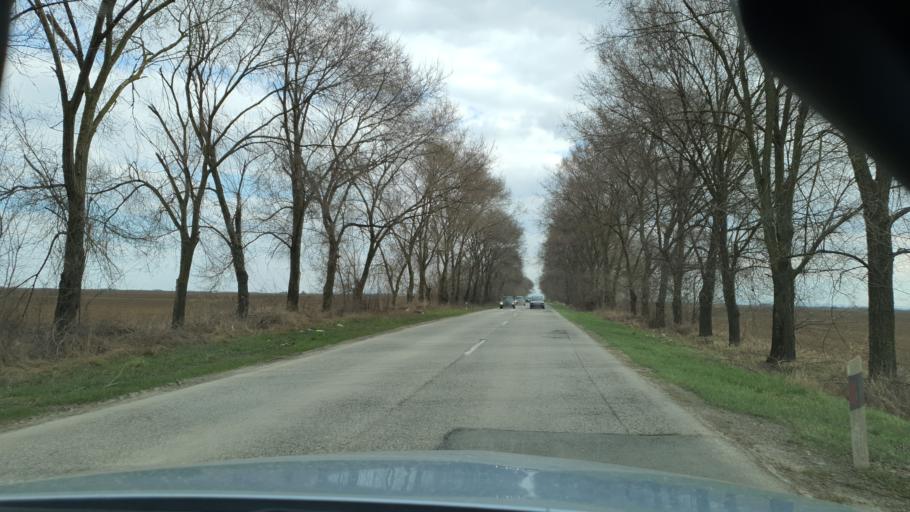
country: RS
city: Obrovac
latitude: 45.4398
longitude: 19.3719
